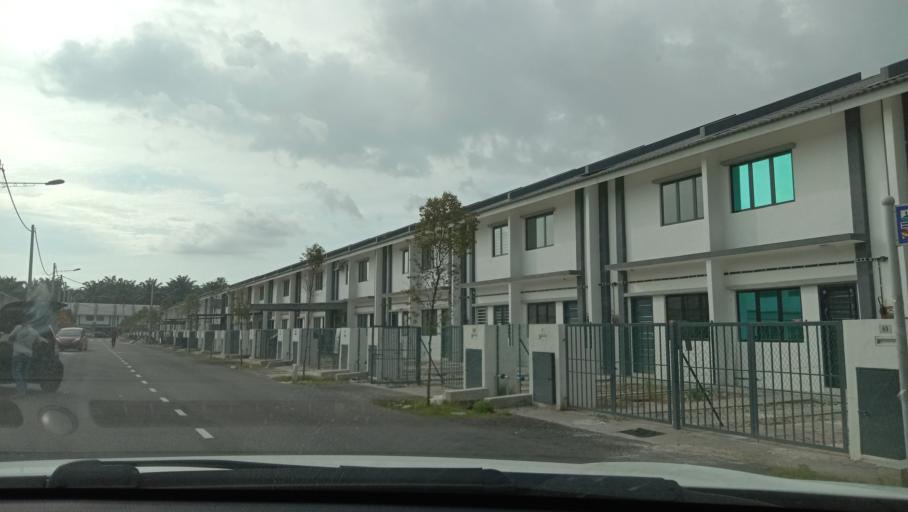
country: MY
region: Selangor
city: Ladang Seri Kundang
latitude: 3.2349
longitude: 101.4791
